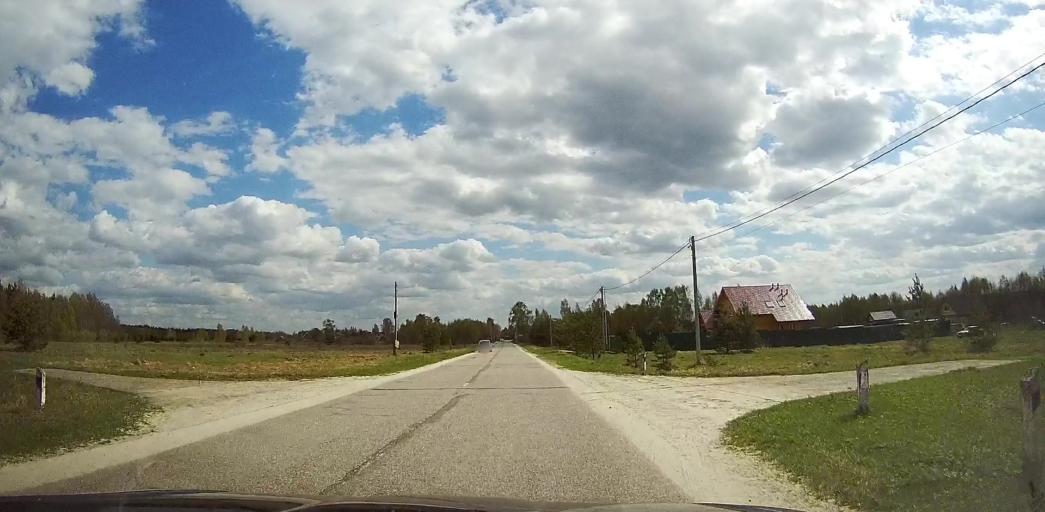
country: RU
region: Moskovskaya
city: Davydovo
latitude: 55.6418
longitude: 38.7752
